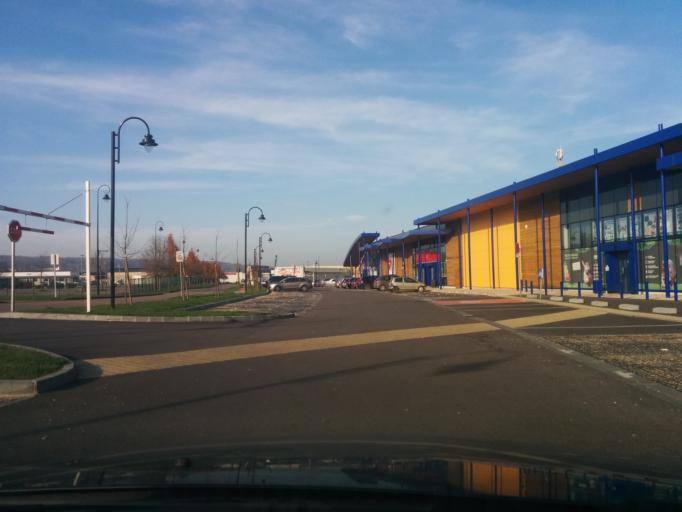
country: FR
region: Haute-Normandie
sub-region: Departement de l'Eure
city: Vernon
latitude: 49.0995
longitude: 1.4590
